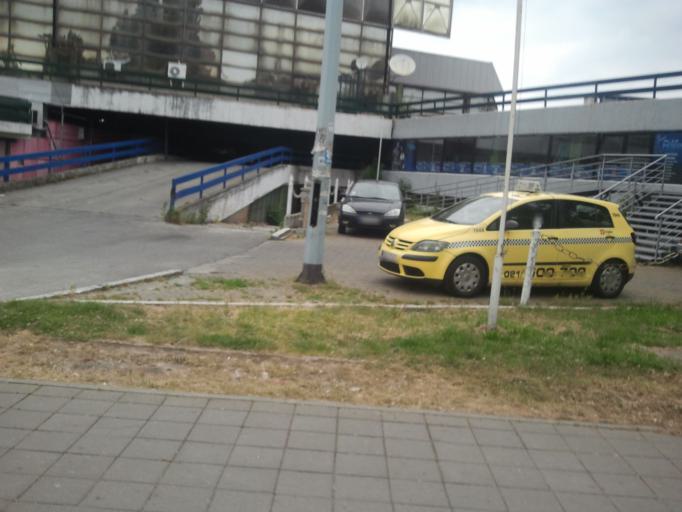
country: RS
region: Autonomna Pokrajina Vojvodina
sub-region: Juznobacki Okrug
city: Novi Sad
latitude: 45.2472
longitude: 19.8470
